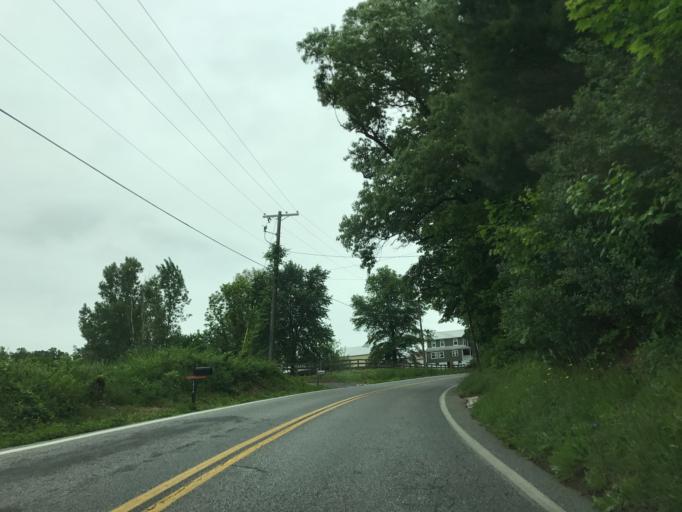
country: US
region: Pennsylvania
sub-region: York County
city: New Freedom
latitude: 39.7079
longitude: -76.6816
